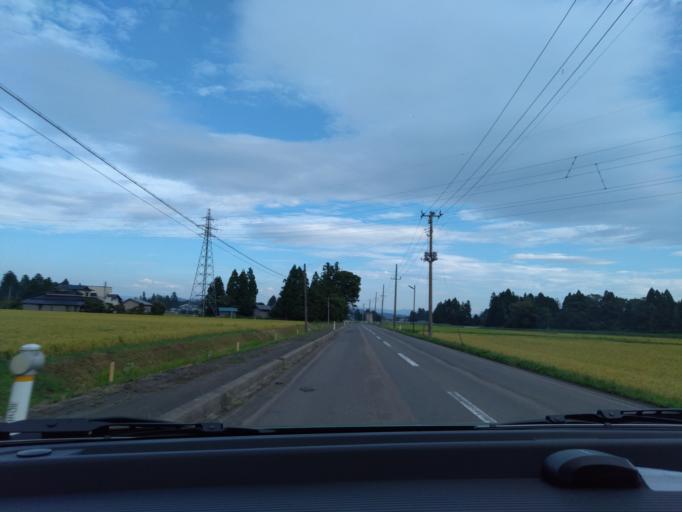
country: JP
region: Iwate
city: Kitakami
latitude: 39.3284
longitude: 141.0577
